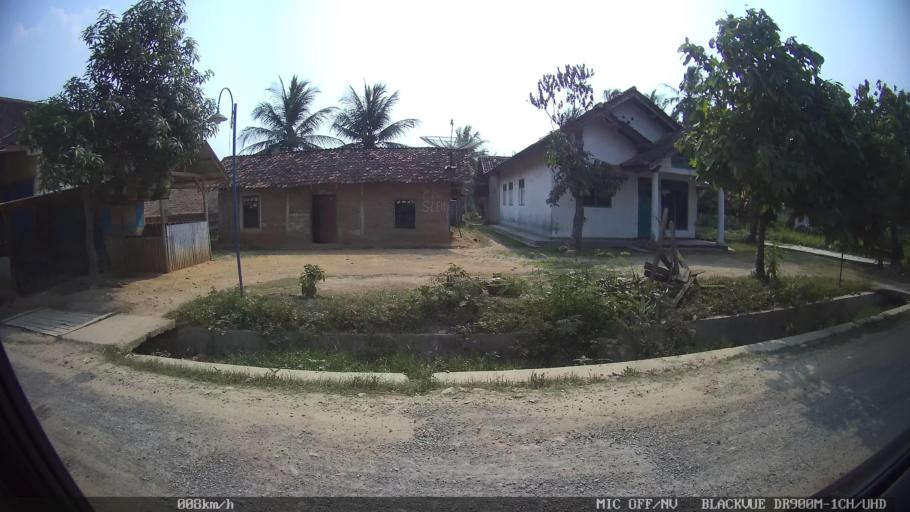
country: ID
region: Lampung
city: Pringsewu
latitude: -5.4076
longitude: 104.9924
